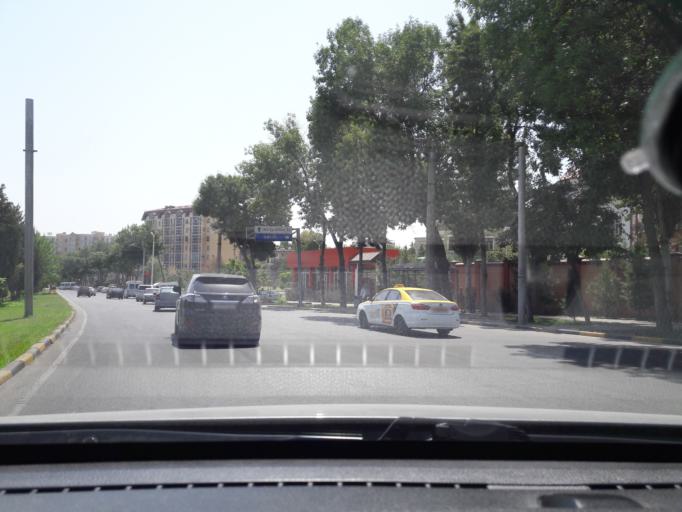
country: TJ
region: Dushanbe
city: Dushanbe
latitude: 38.5919
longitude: 68.7426
